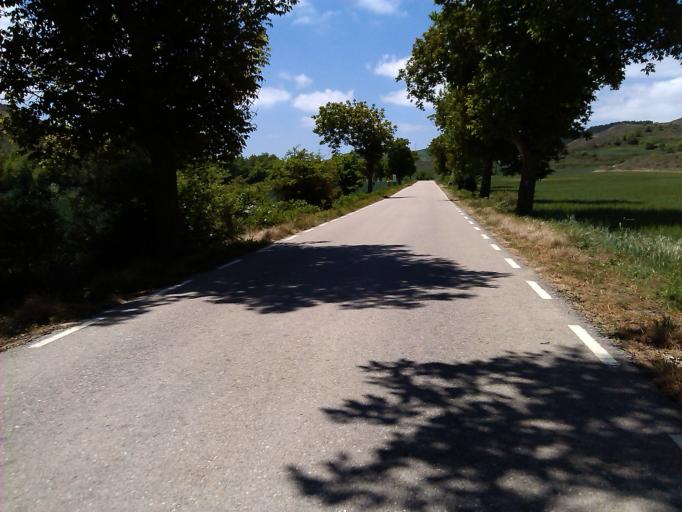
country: ES
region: Castille and Leon
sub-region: Provincia de Burgos
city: Alcocero de Mola
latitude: 42.4489
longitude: -3.3453
